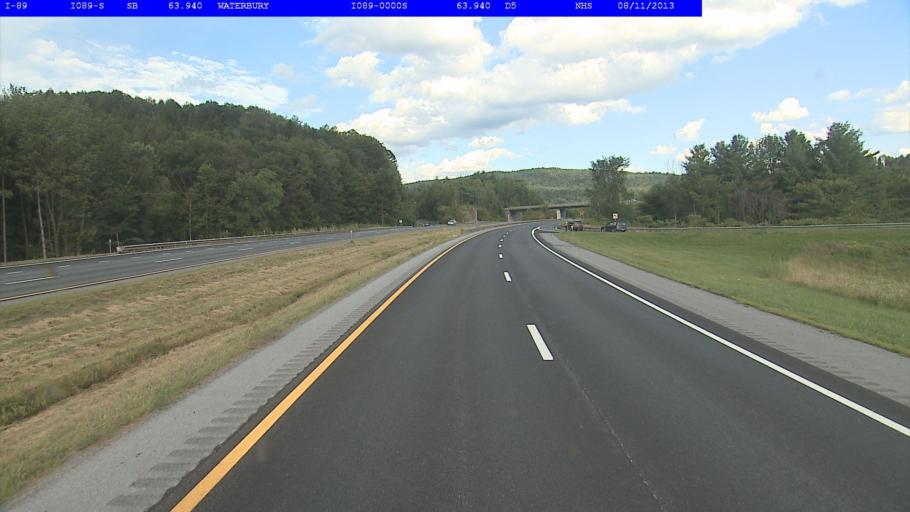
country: US
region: Vermont
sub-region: Washington County
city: Waterbury
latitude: 44.3445
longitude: -72.7558
